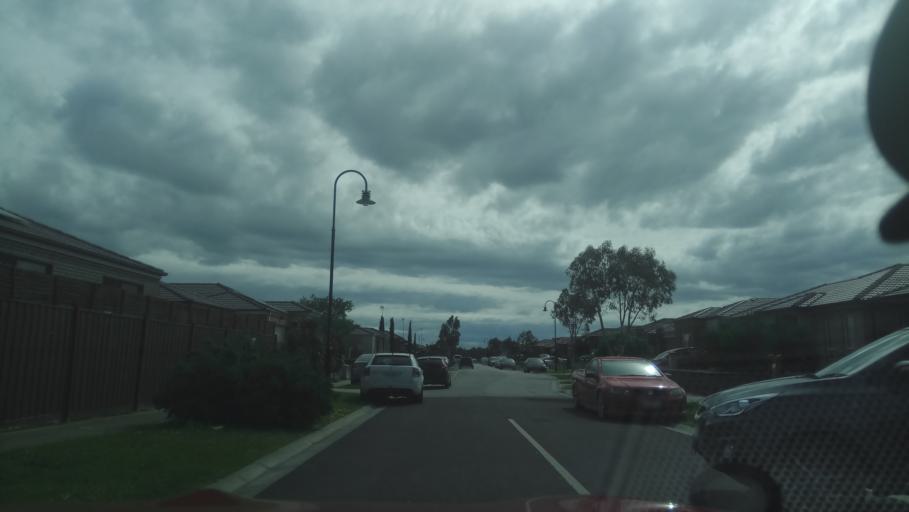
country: AU
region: Victoria
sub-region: Casey
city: Lynbrook
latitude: -38.0727
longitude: 145.2570
